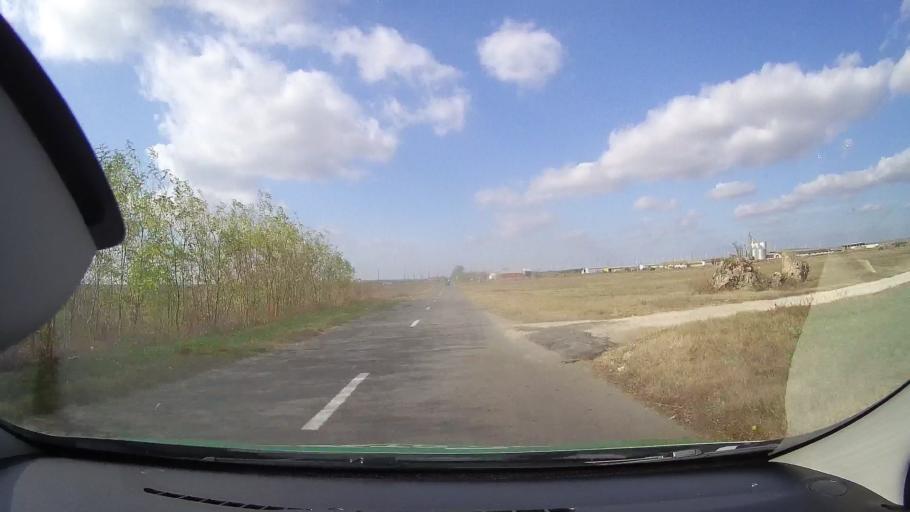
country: RO
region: Constanta
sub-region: Comuna Istria
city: Nuntasi
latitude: 44.5338
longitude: 28.6664
